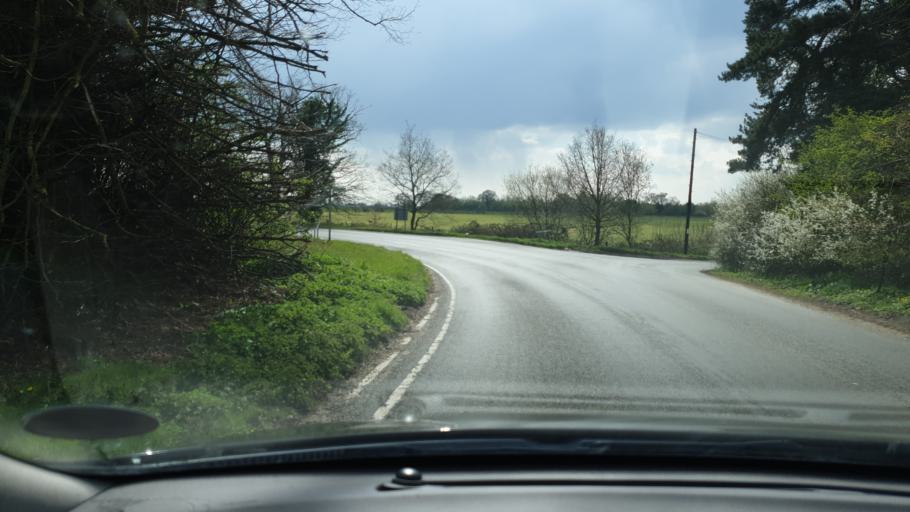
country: GB
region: England
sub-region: Essex
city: Alresford
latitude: 51.9183
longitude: 0.9861
